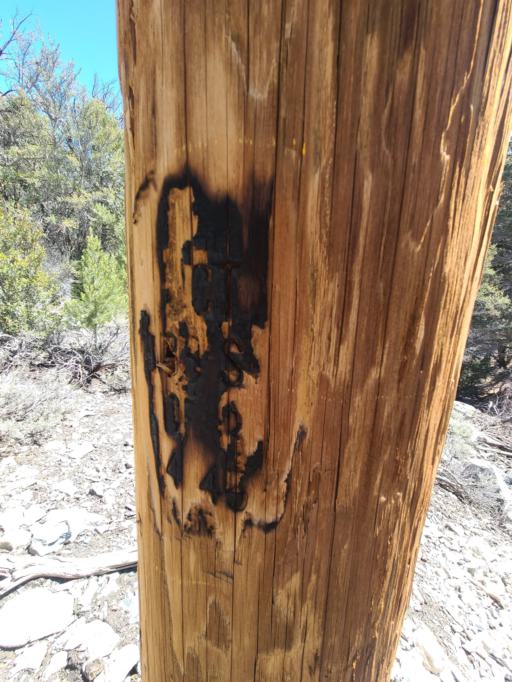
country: US
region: California
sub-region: San Bernardino County
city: Big Bear Lake
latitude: 34.3267
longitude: -116.9371
